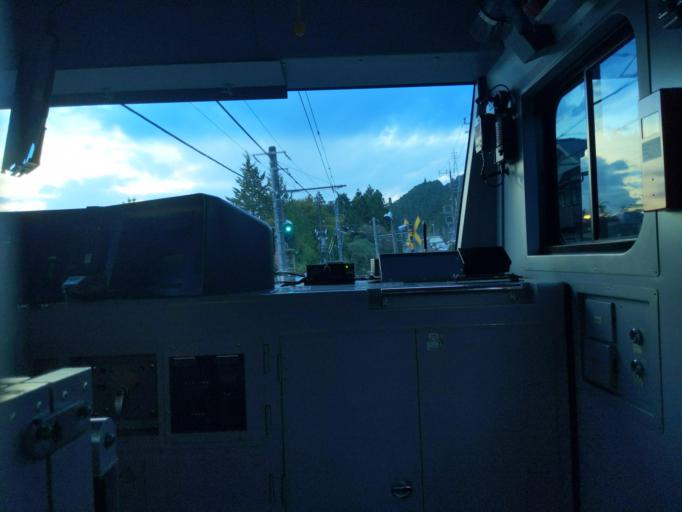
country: JP
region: Tokyo
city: Itsukaichi
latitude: 35.7315
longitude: 139.2456
